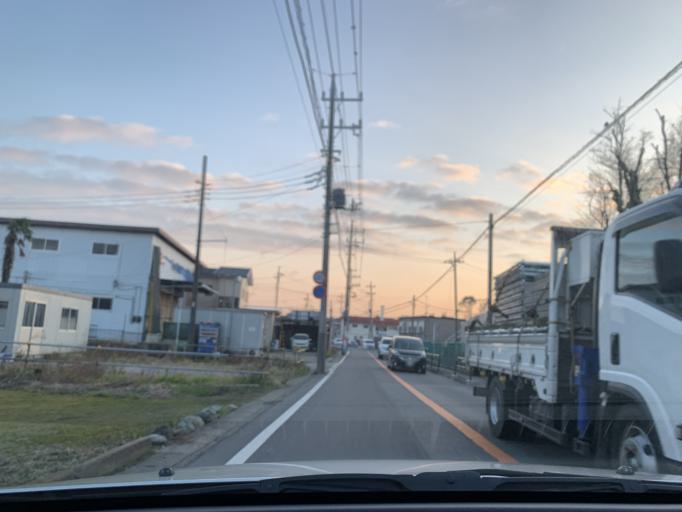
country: JP
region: Chiba
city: Matsudo
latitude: 35.7574
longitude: 139.9185
